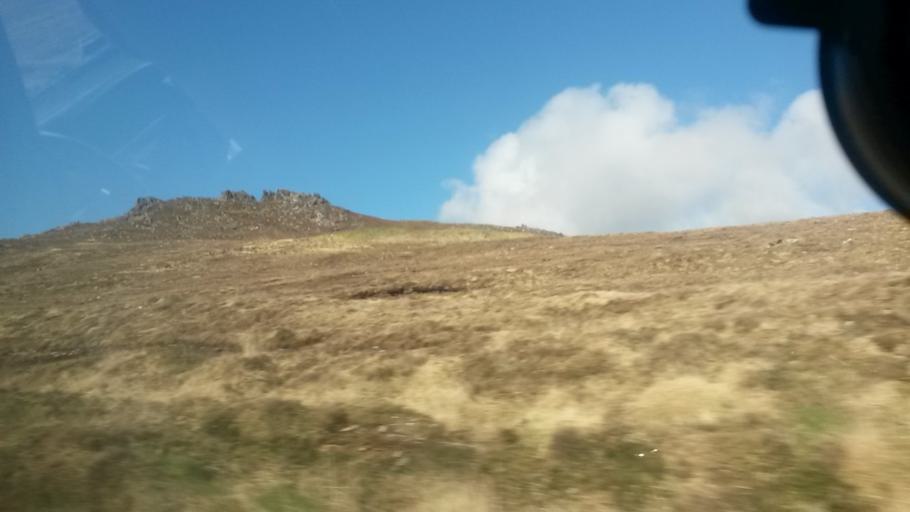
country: IE
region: Munster
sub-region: Ciarrai
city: Dingle
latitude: 52.1438
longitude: -10.4635
